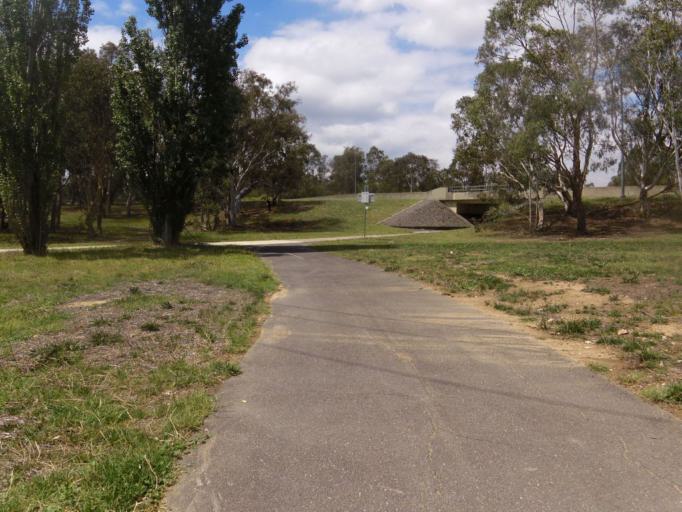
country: AU
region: Australian Capital Territory
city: Macarthur
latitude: -35.4175
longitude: 149.0747
